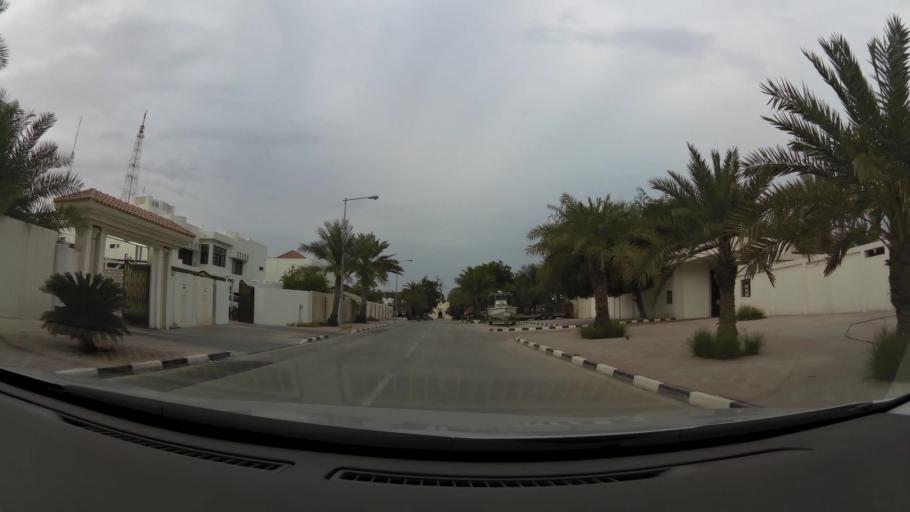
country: QA
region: Baladiyat ad Dawhah
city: Doha
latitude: 25.3345
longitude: 51.5153
